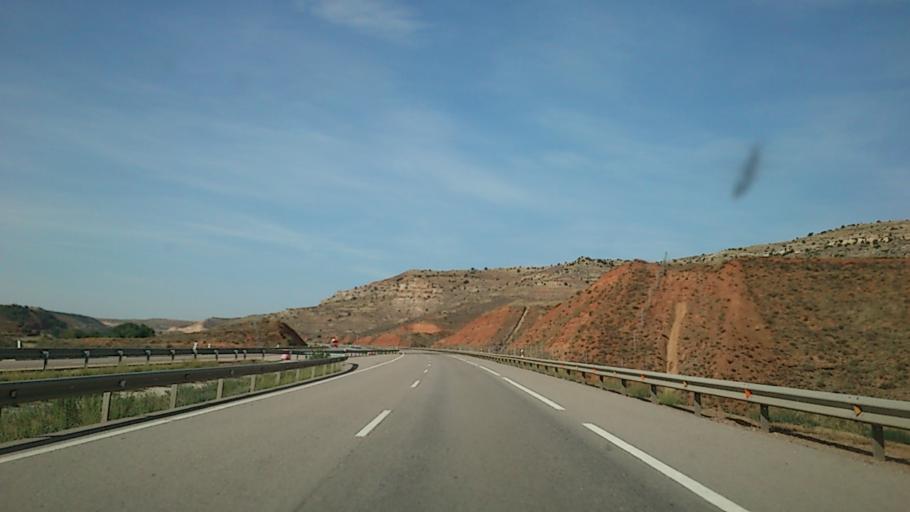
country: ES
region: Aragon
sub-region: Provincia de Teruel
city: Calamocha
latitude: 40.9637
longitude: -1.2624
